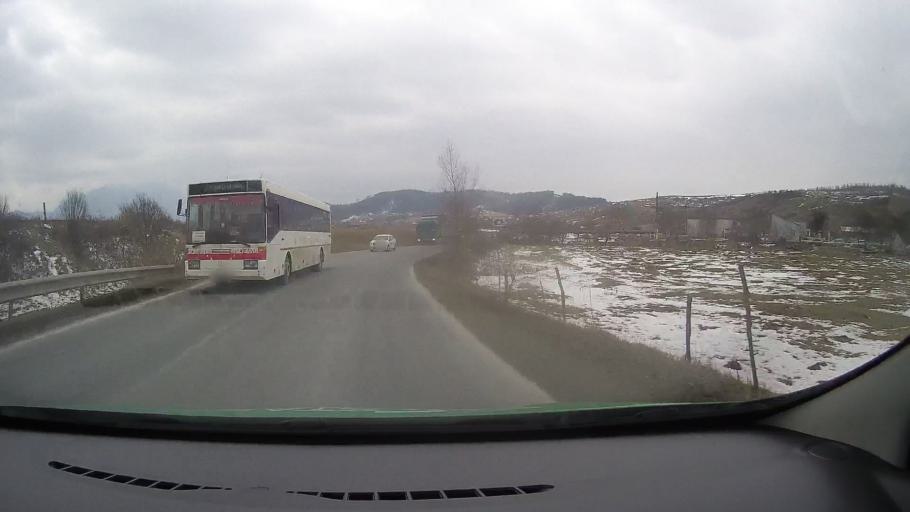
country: RO
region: Brasov
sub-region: Comuna Zarnesti
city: Tohanu Nou
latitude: 45.5776
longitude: 25.3898
